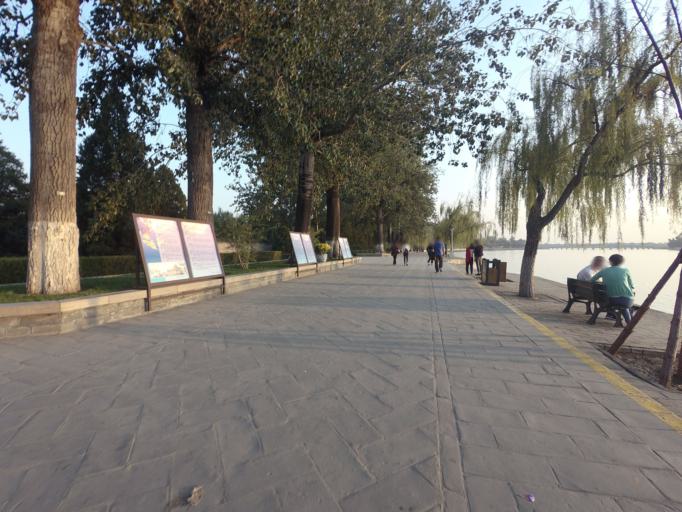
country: CN
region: Beijing
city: Haidian
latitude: 39.9942
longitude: 116.2743
